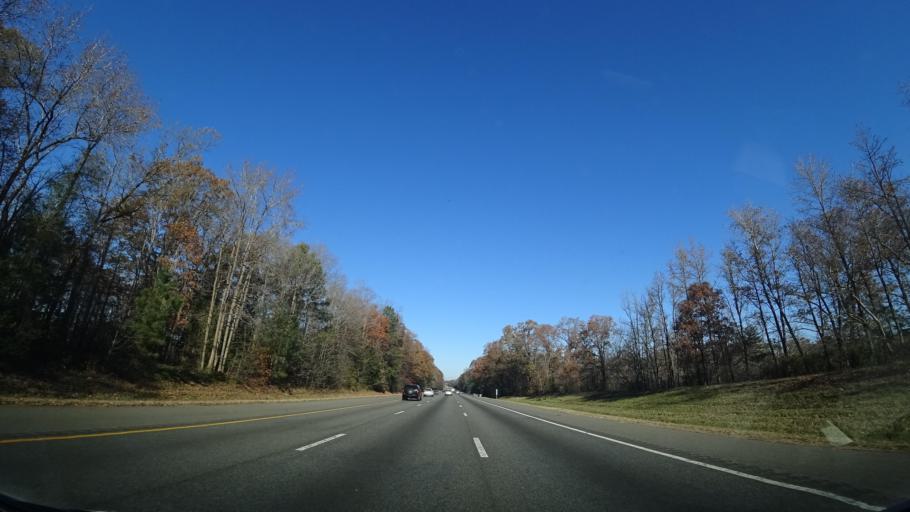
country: US
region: Virginia
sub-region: Caroline County
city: Bowling Green
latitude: 38.0532
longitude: -77.5002
